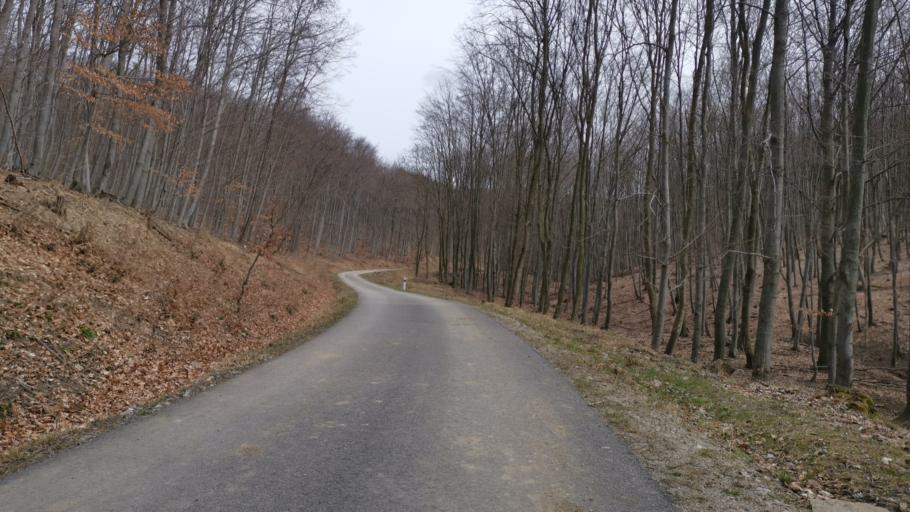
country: CZ
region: South Moravian
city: Straznice
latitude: 48.8153
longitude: 17.3403
